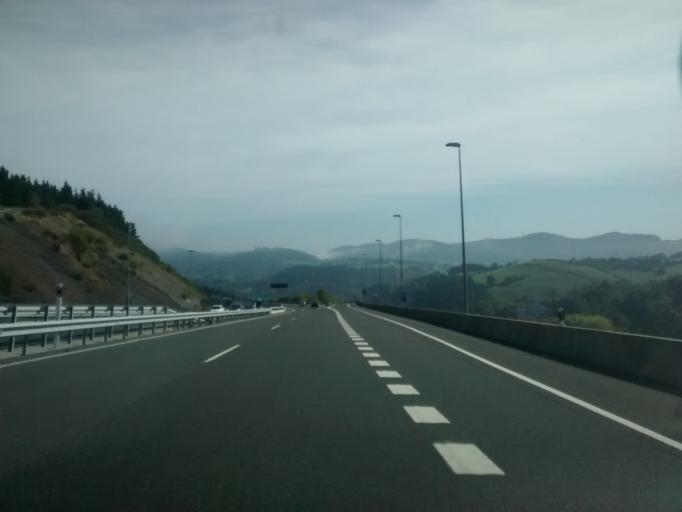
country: ES
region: Basque Country
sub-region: Provincia de Guipuzcoa
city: Eskoriatza
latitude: 43.0241
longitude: -2.5216
